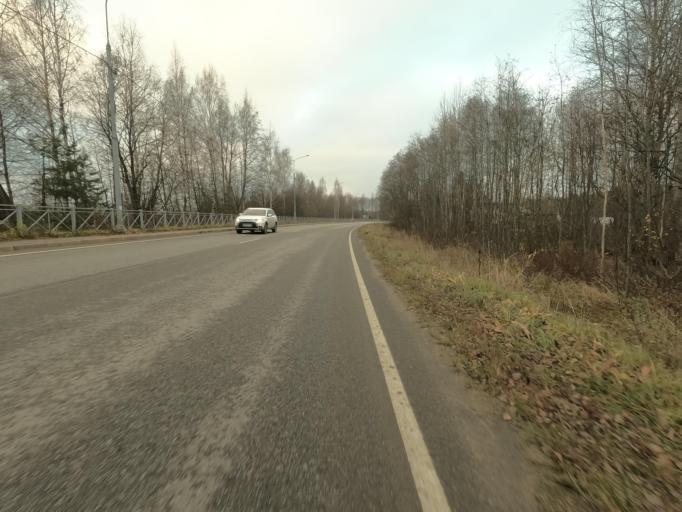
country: RU
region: Leningrad
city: Pavlovo
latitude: 59.8039
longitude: 30.9608
